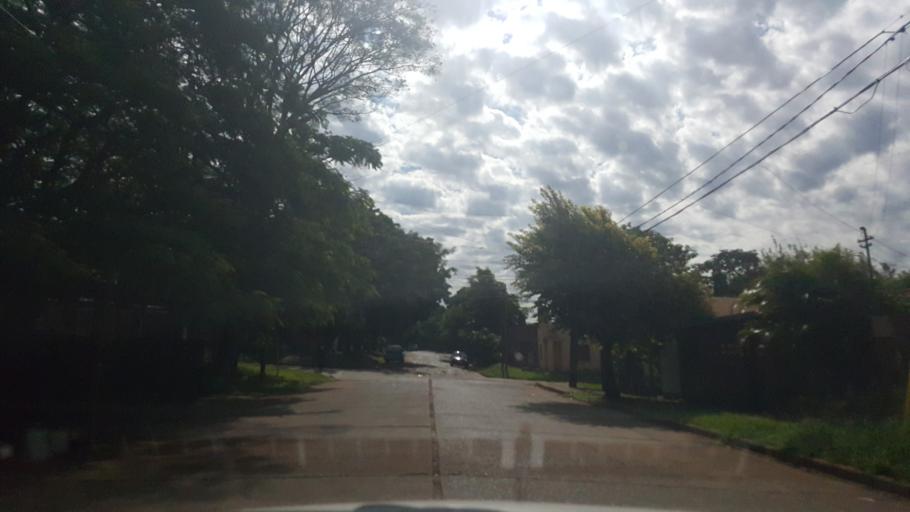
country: AR
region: Misiones
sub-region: Departamento de Capital
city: Posadas
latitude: -27.3675
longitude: -55.9185
